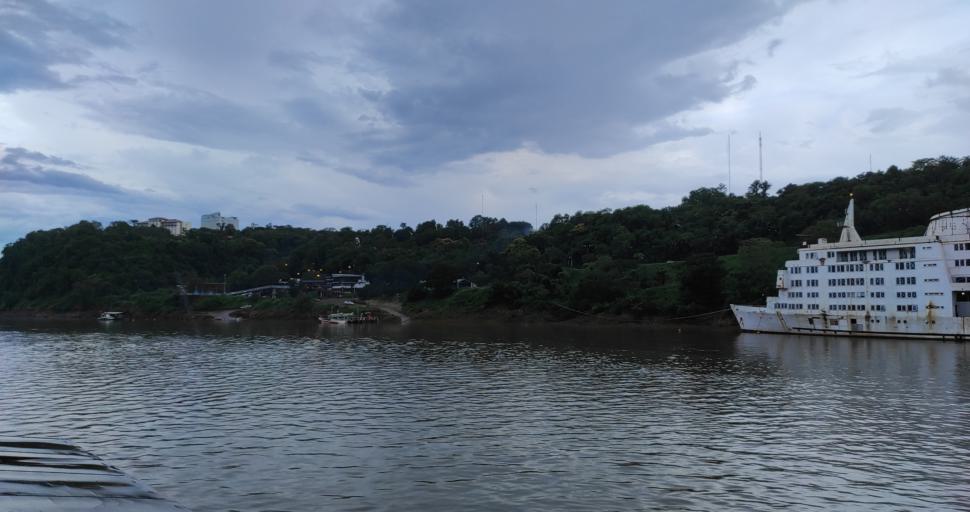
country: AR
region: Misiones
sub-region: Departamento de Iguazu
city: Puerto Iguazu
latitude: -25.5924
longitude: -54.5828
